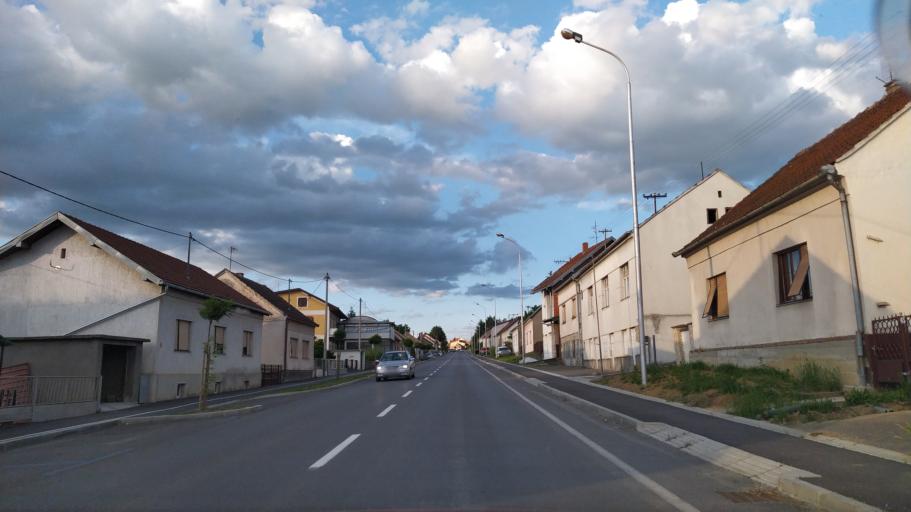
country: HR
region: Osjecko-Baranjska
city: Nasice
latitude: 45.4870
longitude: 18.0801
